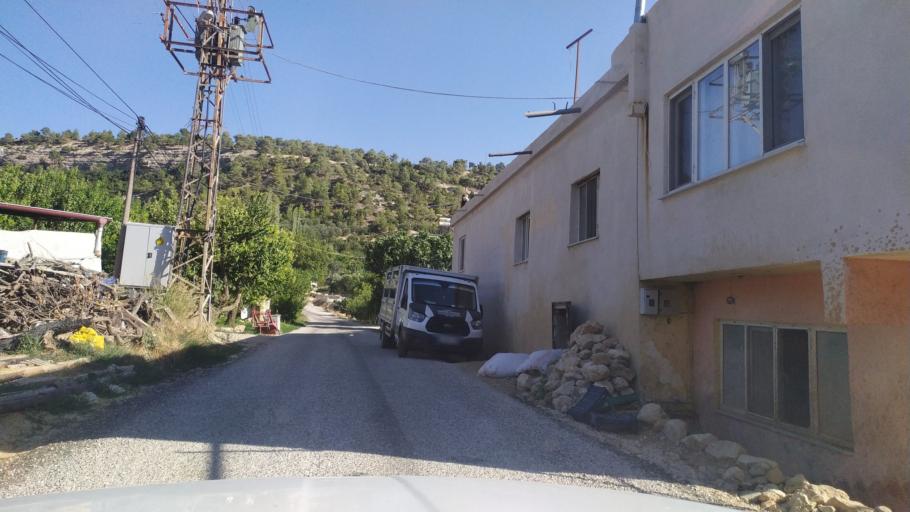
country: TR
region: Mersin
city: Mut
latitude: 36.7070
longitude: 33.4730
